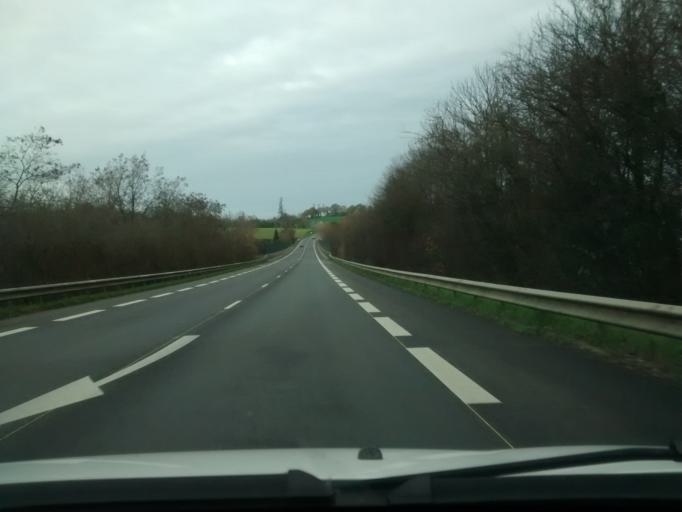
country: FR
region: Brittany
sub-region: Departement d'Ille-et-Vilaine
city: Poce-les-Bois
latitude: 48.1171
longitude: -1.2296
